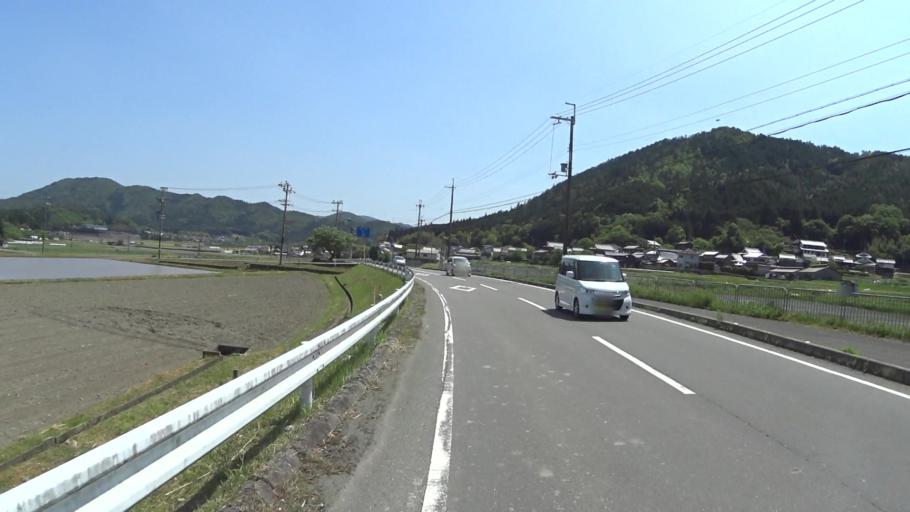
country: JP
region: Kyoto
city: Kameoka
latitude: 35.0290
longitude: 135.4849
